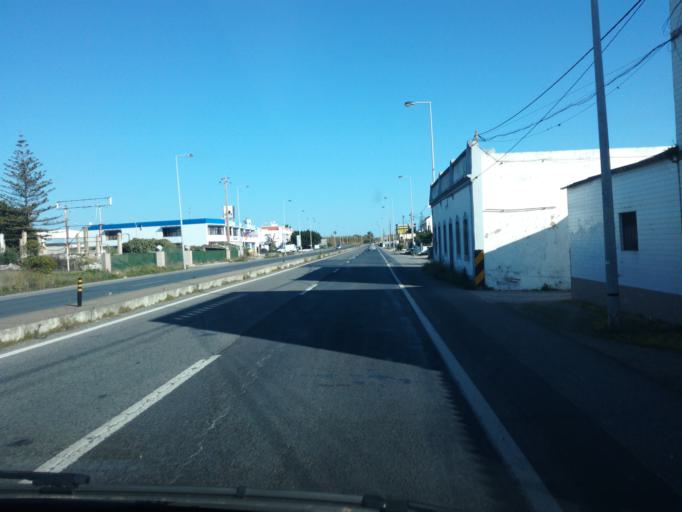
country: PT
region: Faro
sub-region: Olhao
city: Olhao
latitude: 37.0299
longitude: -7.8724
